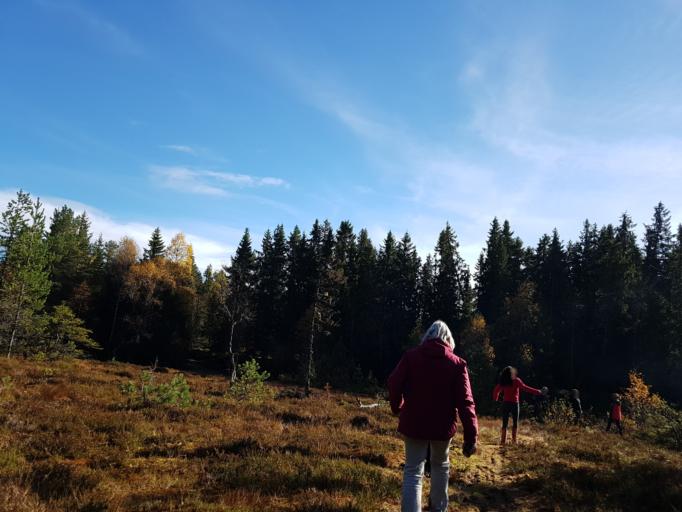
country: NO
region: Sor-Trondelag
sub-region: Trondheim
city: Trondheim
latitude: 63.4221
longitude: 10.2971
